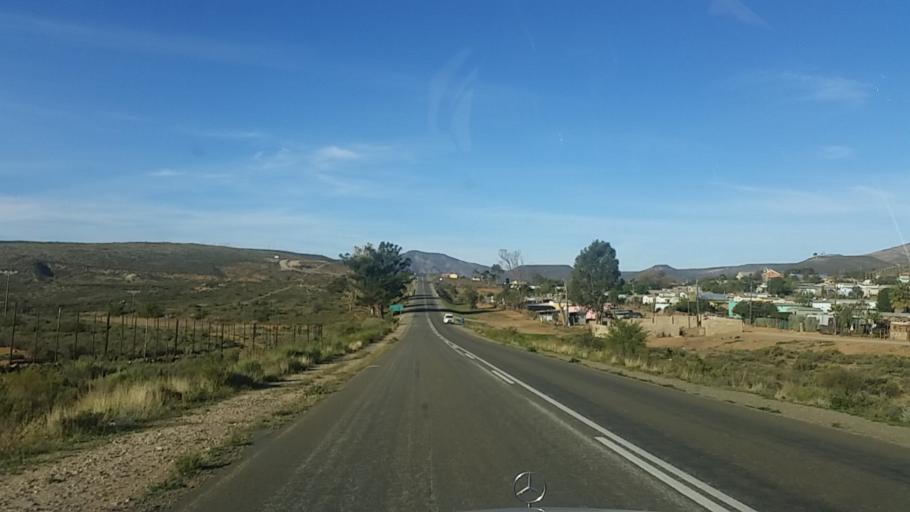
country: ZA
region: Western Cape
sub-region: Eden District Municipality
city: Knysna
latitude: -33.6638
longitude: 23.1069
